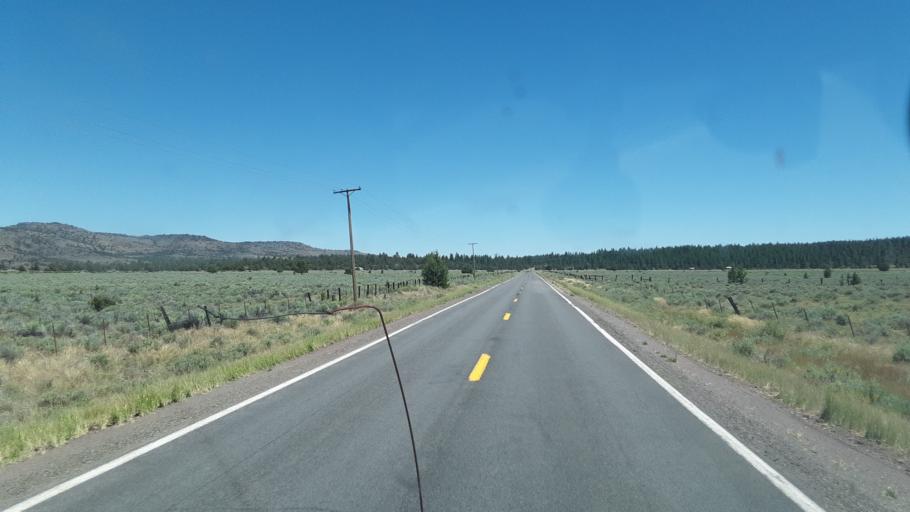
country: US
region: California
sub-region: Lassen County
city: Susanville
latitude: 40.5251
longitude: -120.5945
